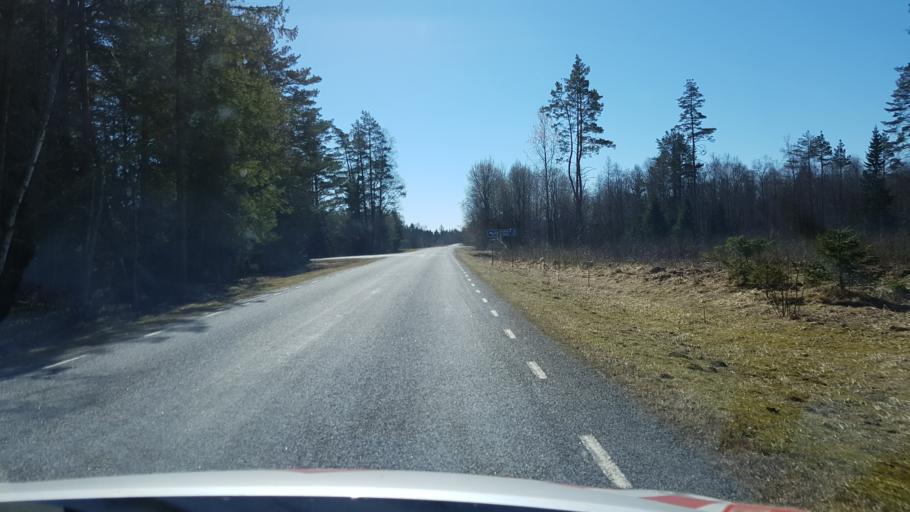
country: EE
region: Laeaene-Virumaa
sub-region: Haljala vald
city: Haljala
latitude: 59.4948
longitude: 26.2436
